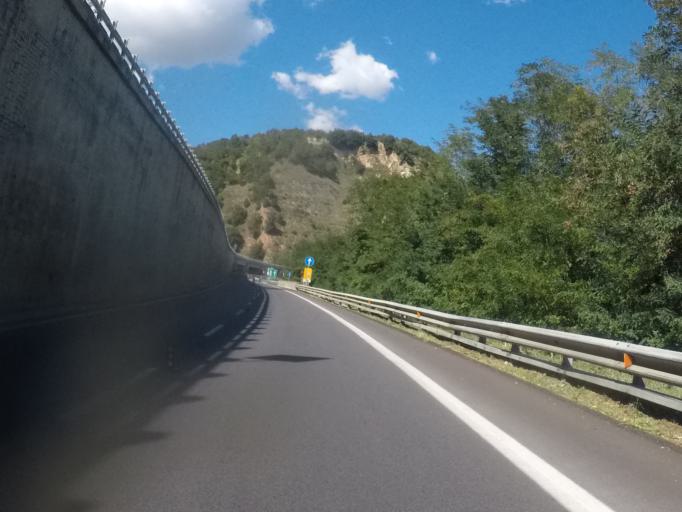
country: IT
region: Calabria
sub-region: Provincia di Cosenza
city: Altilia
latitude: 39.1400
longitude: 16.2747
